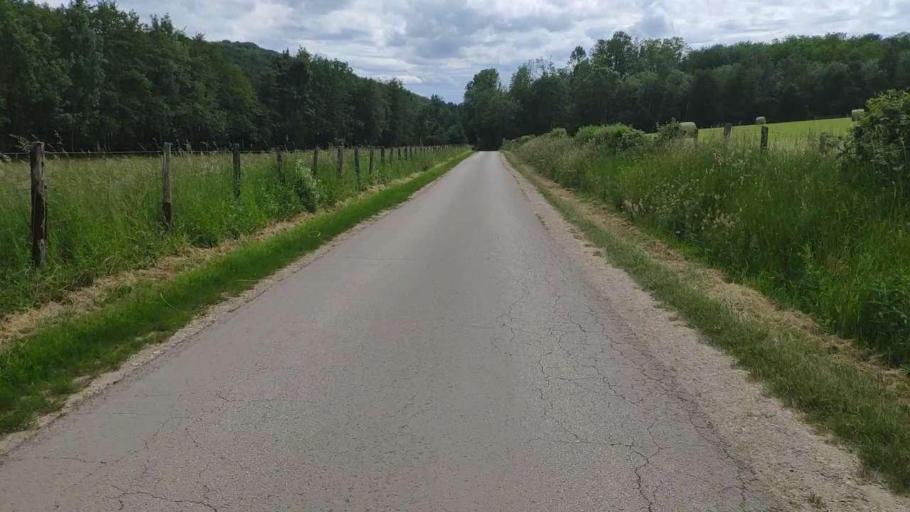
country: FR
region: Franche-Comte
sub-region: Departement du Jura
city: Montmorot
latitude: 46.7408
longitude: 5.5313
